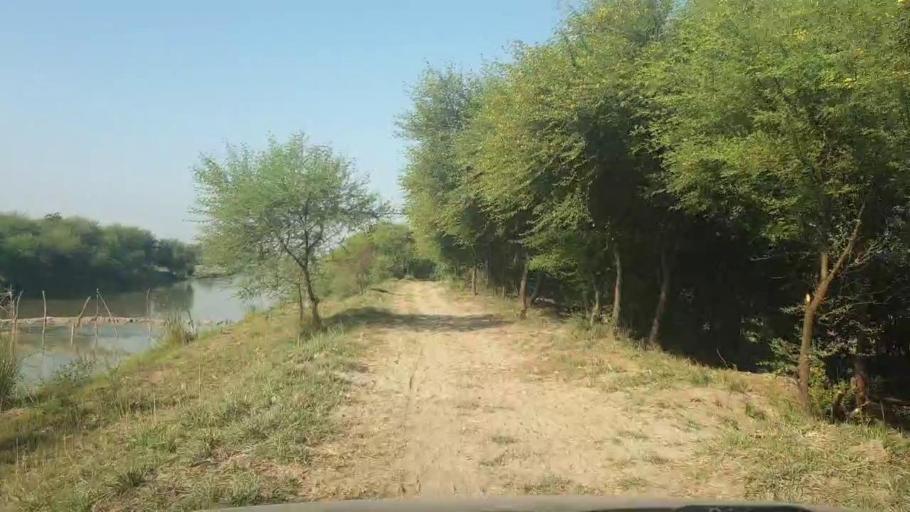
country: PK
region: Sindh
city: Badin
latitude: 24.7138
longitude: 68.9018
